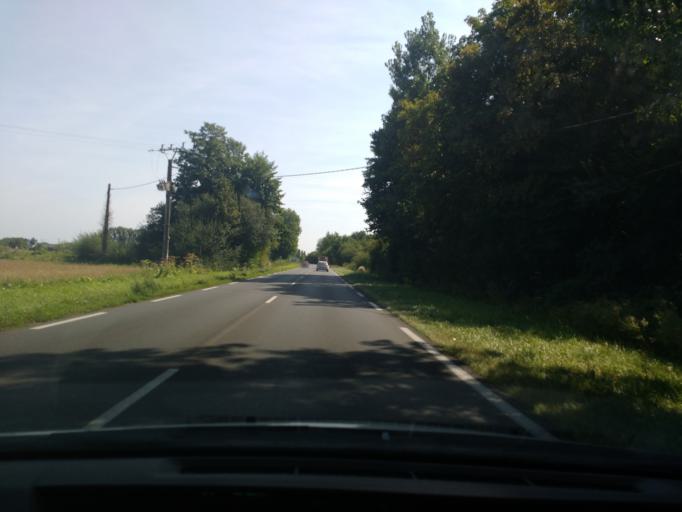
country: FR
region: Pays de la Loire
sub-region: Departement de Maine-et-Loire
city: Andard
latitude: 47.4652
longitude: -0.3927
